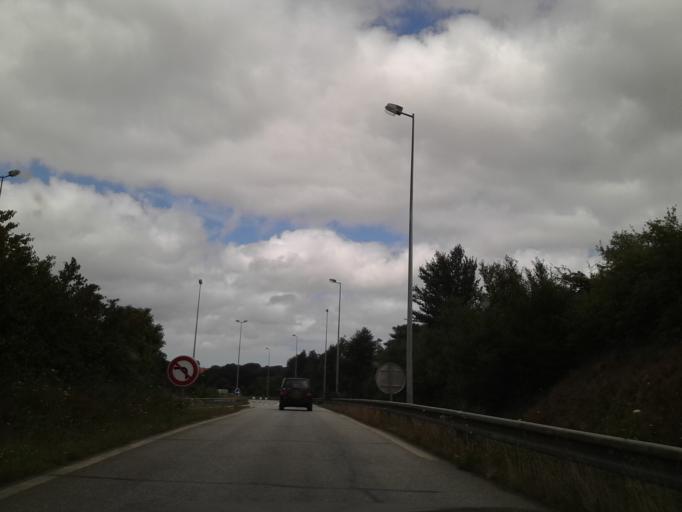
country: FR
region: Lower Normandy
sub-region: Departement de la Manche
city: La Glacerie
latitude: 49.6006
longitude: -1.5946
